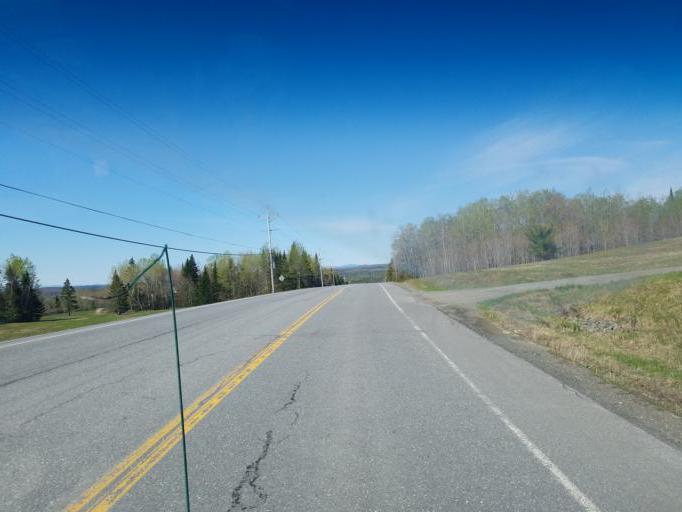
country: US
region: Maine
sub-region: Aroostook County
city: Presque Isle
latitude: 46.6638
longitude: -68.2287
